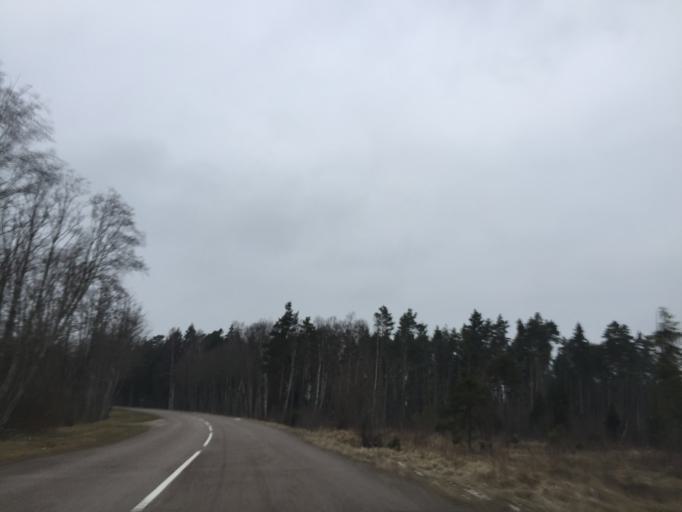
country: EE
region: Saare
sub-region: Kuressaare linn
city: Kuressaare
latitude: 58.3858
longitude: 22.2313
